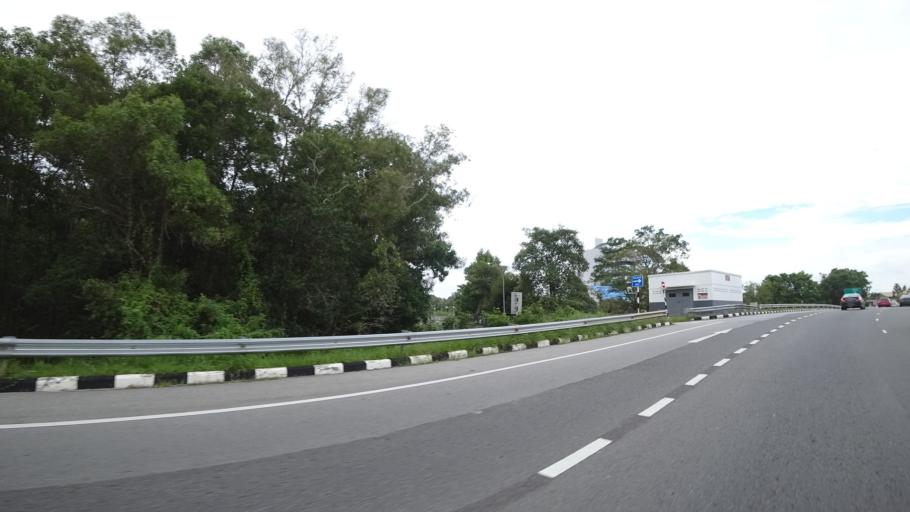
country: BN
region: Brunei and Muara
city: Bandar Seri Begawan
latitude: 4.8983
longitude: 114.9019
